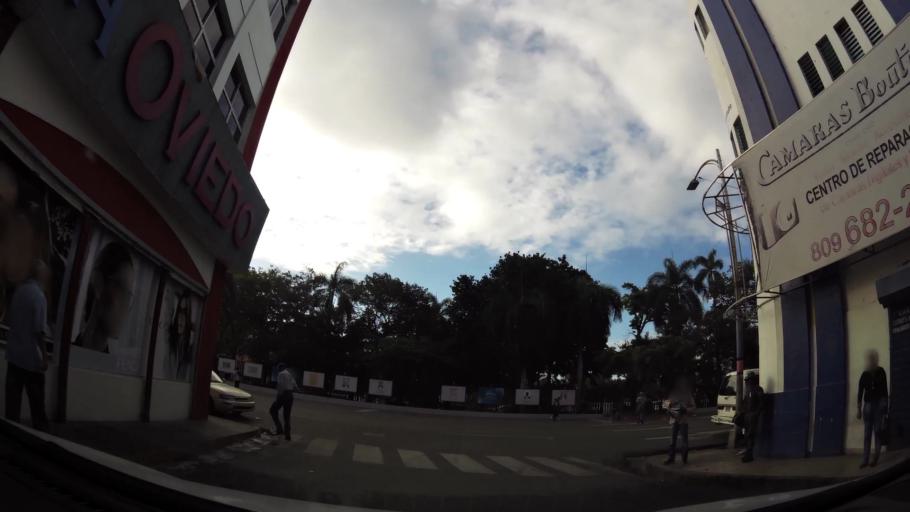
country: DO
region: Nacional
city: Ciudad Nueva
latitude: 18.4719
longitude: -69.8923
